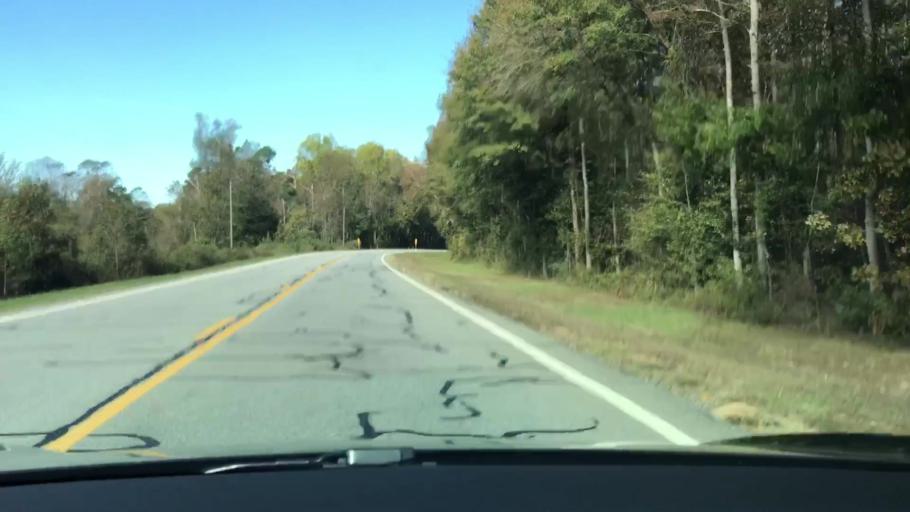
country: US
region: Georgia
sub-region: Glascock County
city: Gibson
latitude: 33.3331
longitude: -82.5658
